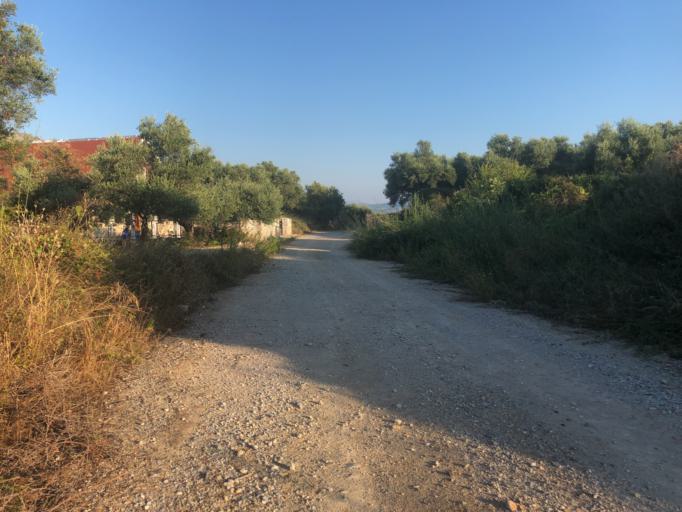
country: GR
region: Crete
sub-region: Nomos Chanias
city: Georgioupolis
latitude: 35.3332
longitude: 24.2922
